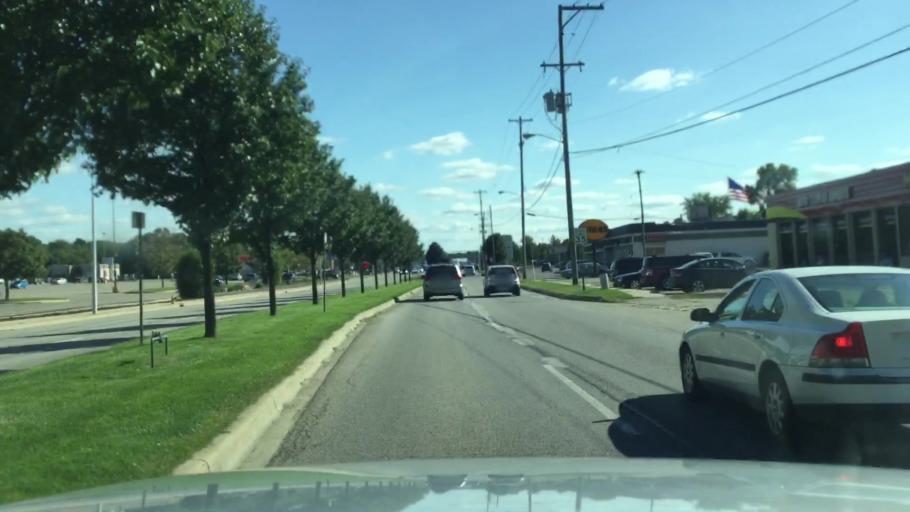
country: US
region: Michigan
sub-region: Kalamazoo County
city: Portage
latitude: 42.2435
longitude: -85.5896
